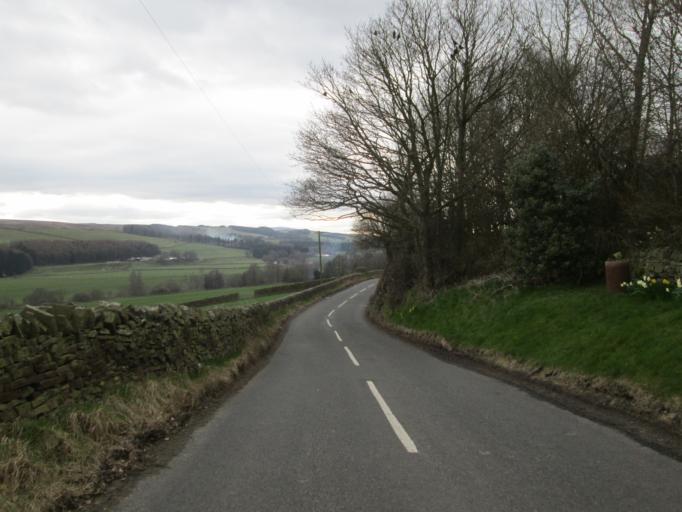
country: GB
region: England
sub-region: Northumberland
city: Bardon Mill
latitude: 54.9698
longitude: -2.3957
